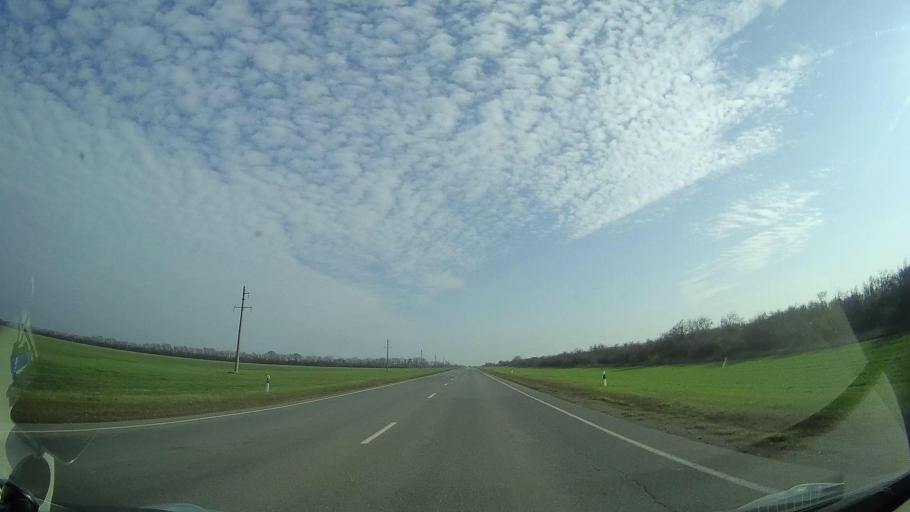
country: RU
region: Rostov
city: Gigant
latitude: 46.5252
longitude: 41.2432
